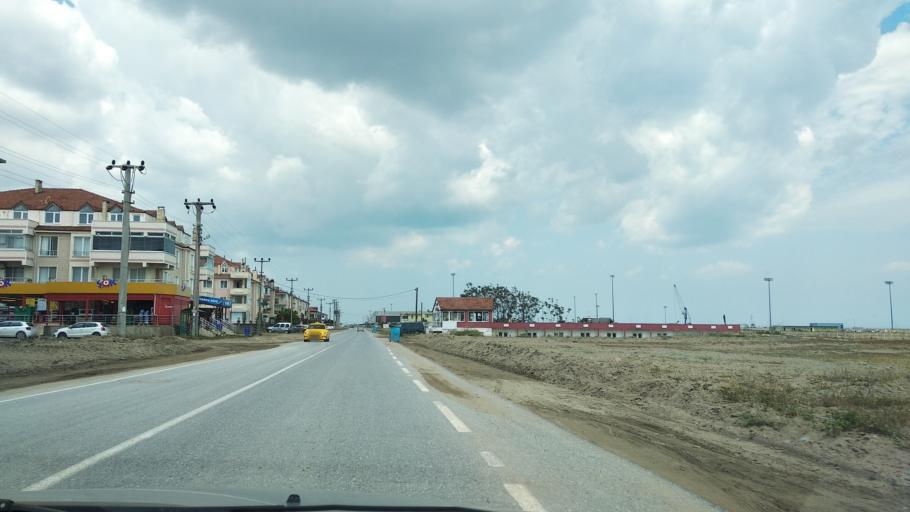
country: TR
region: Sakarya
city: Karasu
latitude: 41.1145
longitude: 30.6808
